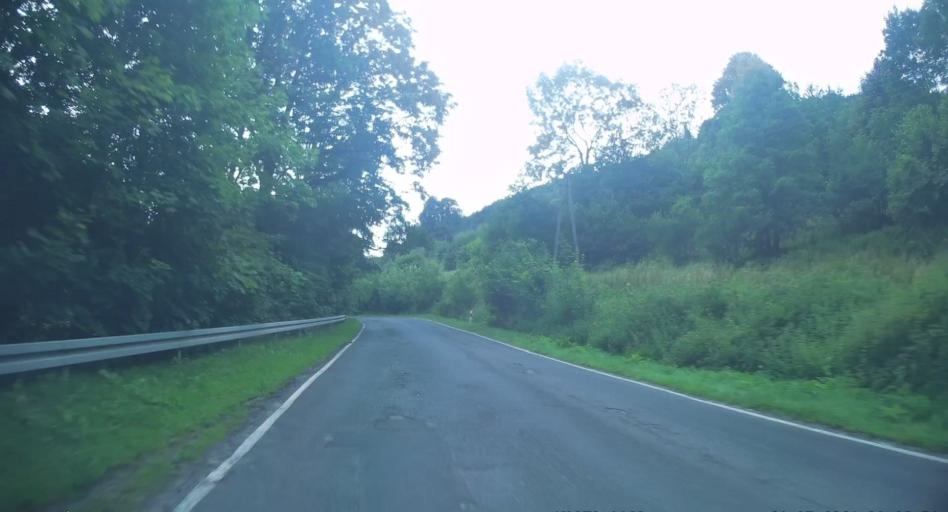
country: PL
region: Lower Silesian Voivodeship
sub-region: Powiat walbrzyski
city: Walim
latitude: 50.7133
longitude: 16.4342
